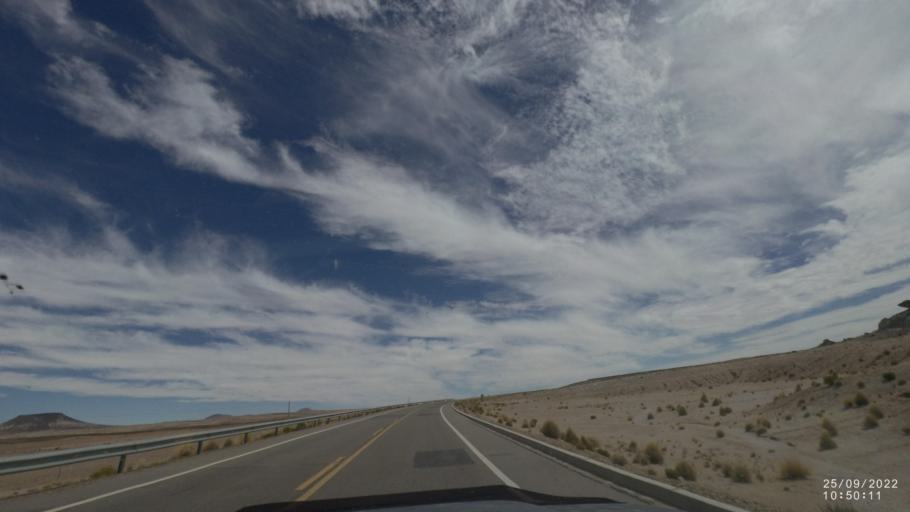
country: BO
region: Oruro
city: Challapata
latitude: -19.5793
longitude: -66.8353
